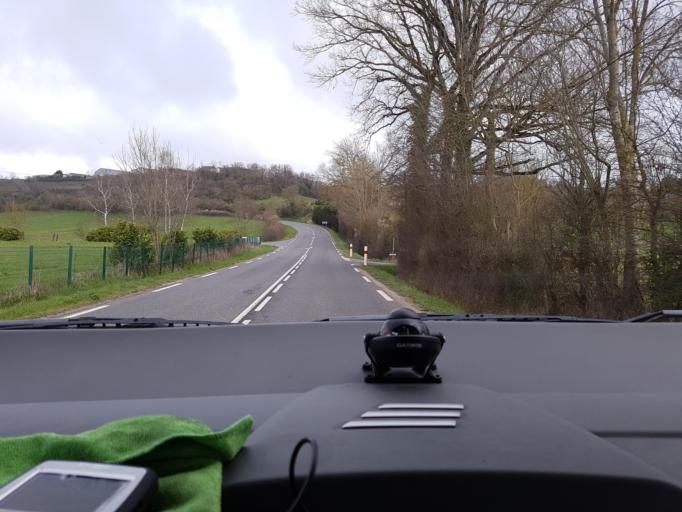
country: FR
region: Midi-Pyrenees
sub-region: Departement de l'Aveyron
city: Olemps
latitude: 44.3671
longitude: 2.5410
